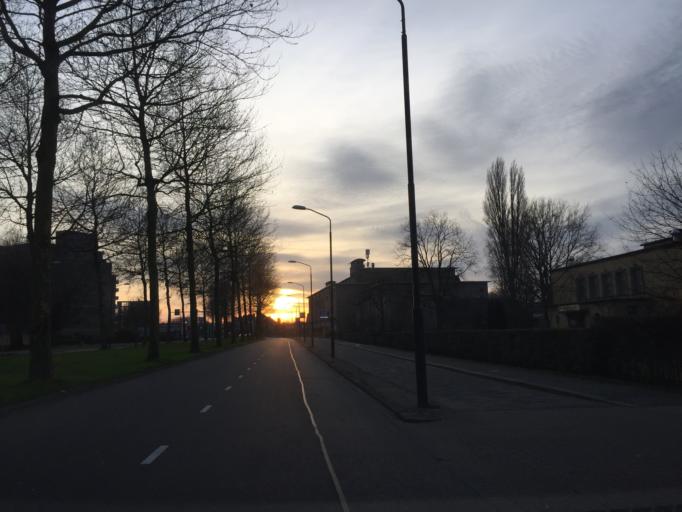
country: NL
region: South Holland
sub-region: Gemeente Dordrecht
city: Dordrecht
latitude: 51.8150
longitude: 4.6867
